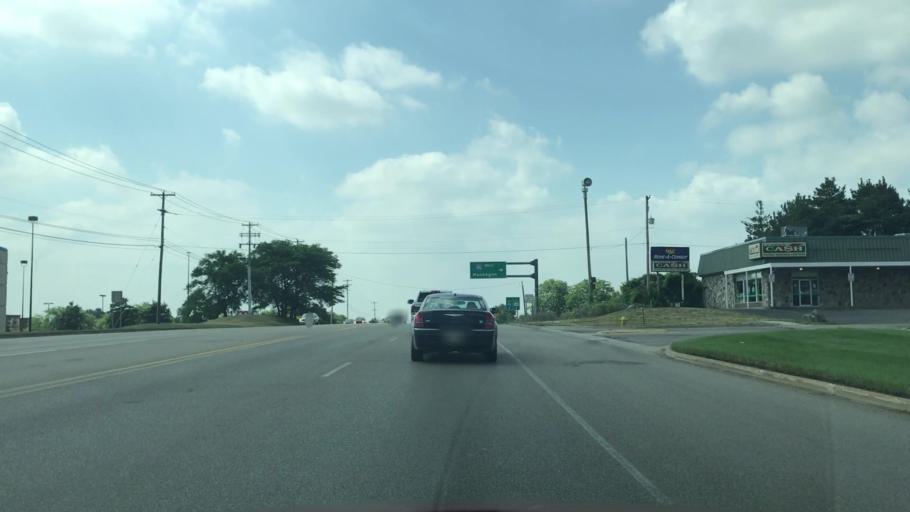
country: US
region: Michigan
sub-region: Kent County
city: Comstock Park
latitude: 43.0207
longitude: -85.6891
